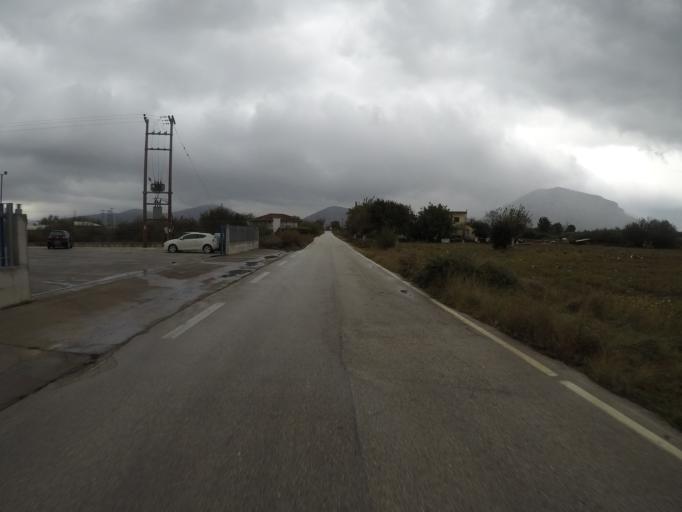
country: GR
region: Peloponnese
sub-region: Nomos Arkadias
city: Tripoli
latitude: 37.5737
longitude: 22.4118
